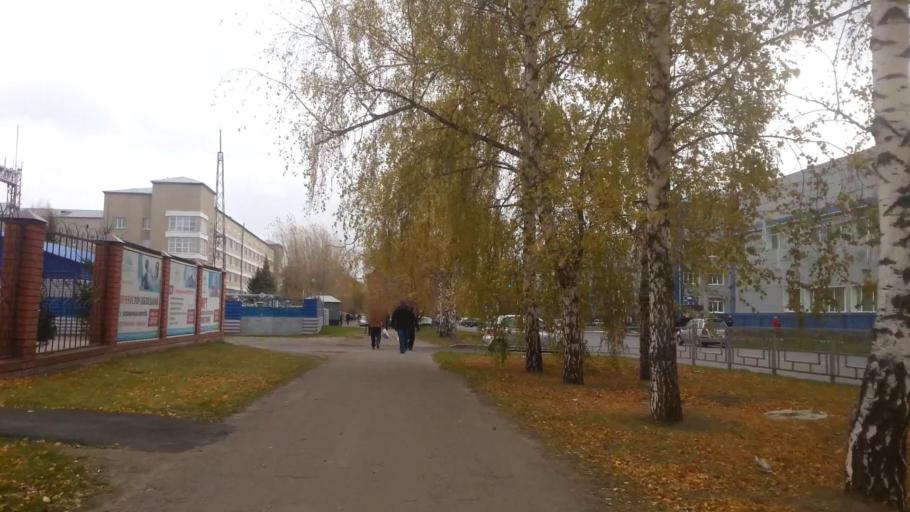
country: RU
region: Altai Krai
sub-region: Gorod Barnaulskiy
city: Barnaul
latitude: 53.3661
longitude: 83.7139
